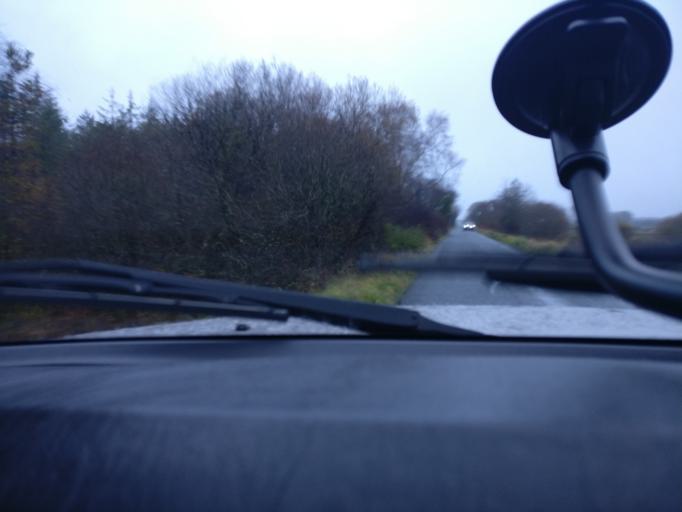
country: IE
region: Connaught
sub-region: County Galway
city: Loughrea
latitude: 53.2336
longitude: -8.5250
